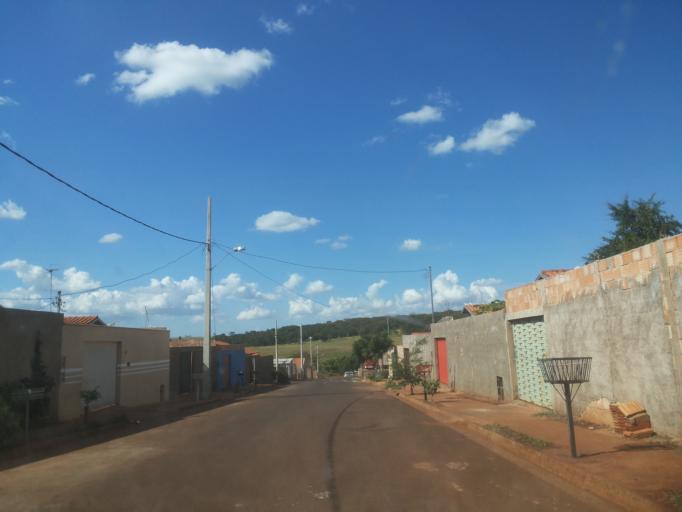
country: BR
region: Minas Gerais
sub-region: Capinopolis
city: Capinopolis
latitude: -18.6872
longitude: -49.5623
